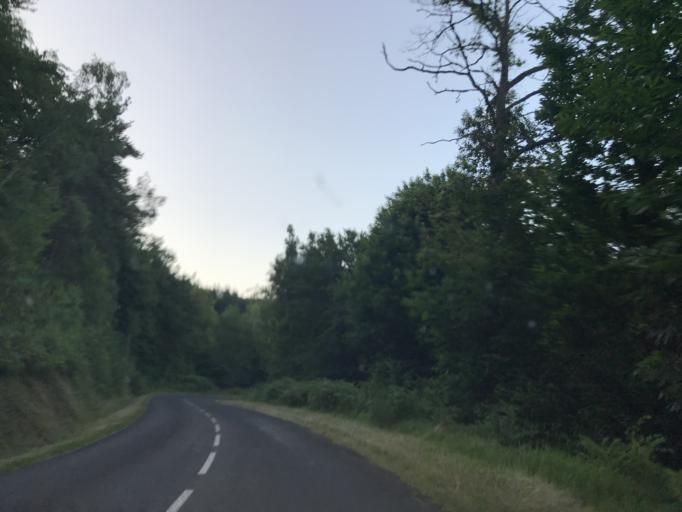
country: FR
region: Auvergne
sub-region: Departement du Puy-de-Dome
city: Courpiere
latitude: 45.7404
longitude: 3.6455
